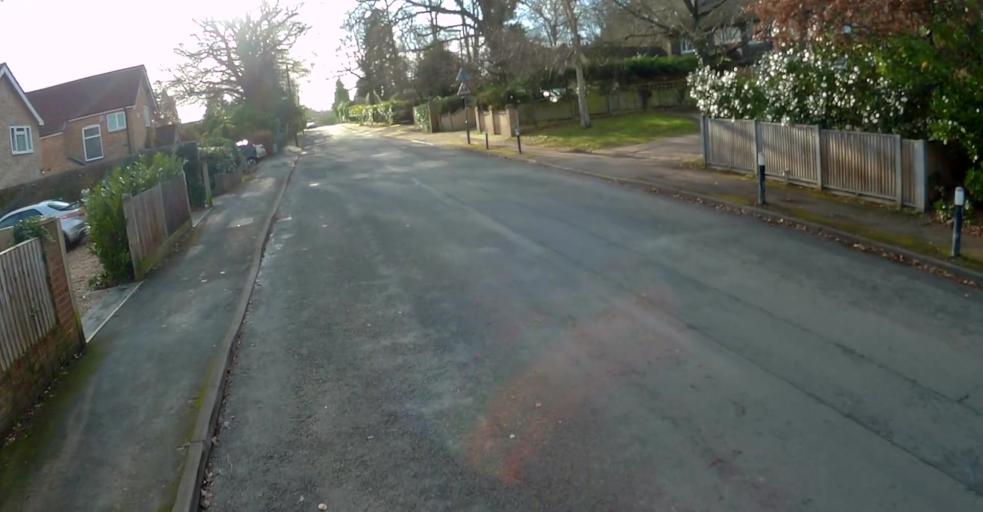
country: GB
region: England
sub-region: Surrey
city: Ottershaw
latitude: 51.3619
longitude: -0.5281
